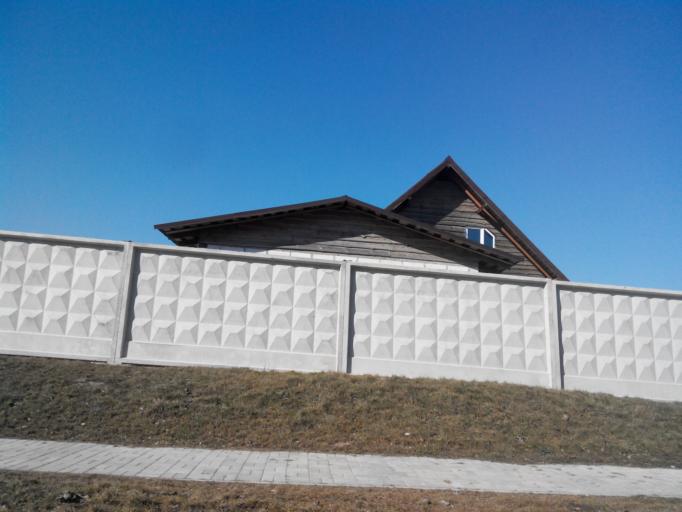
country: BY
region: Minsk
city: Zhdanovichy
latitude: 53.9184
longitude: 27.4111
